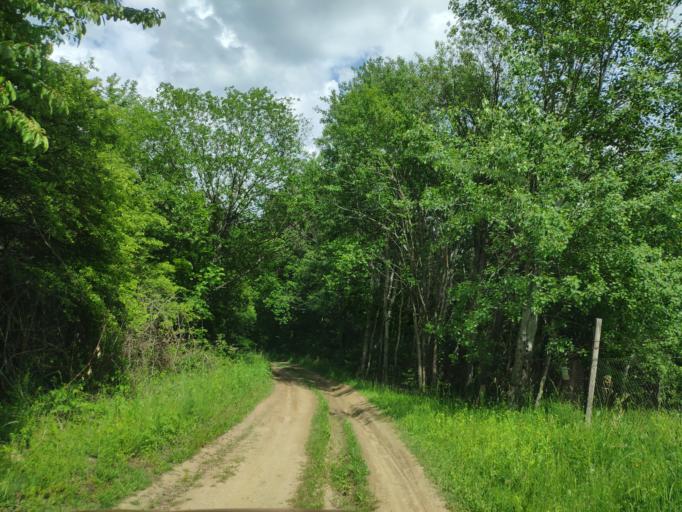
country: SK
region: Kosicky
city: Medzev
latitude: 48.7213
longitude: 20.9625
